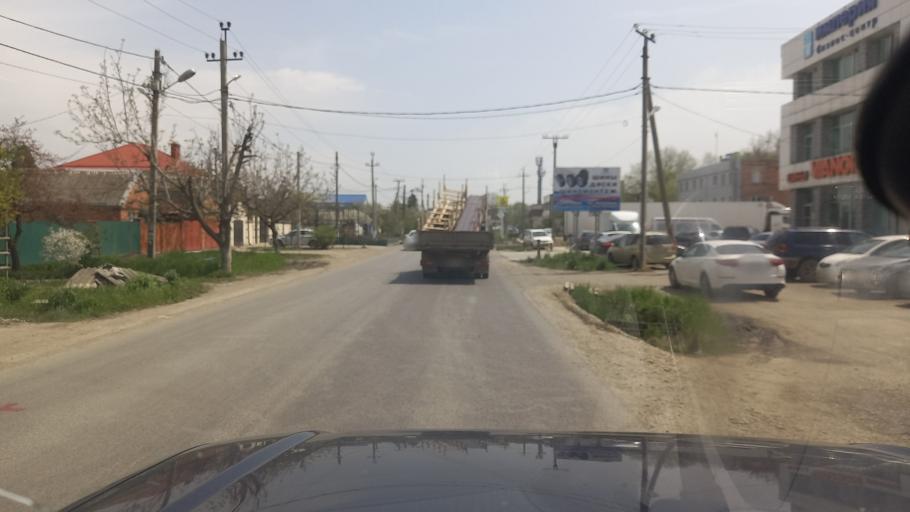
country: RU
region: Adygeya
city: Yablonovskiy
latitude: 44.9881
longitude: 38.9574
